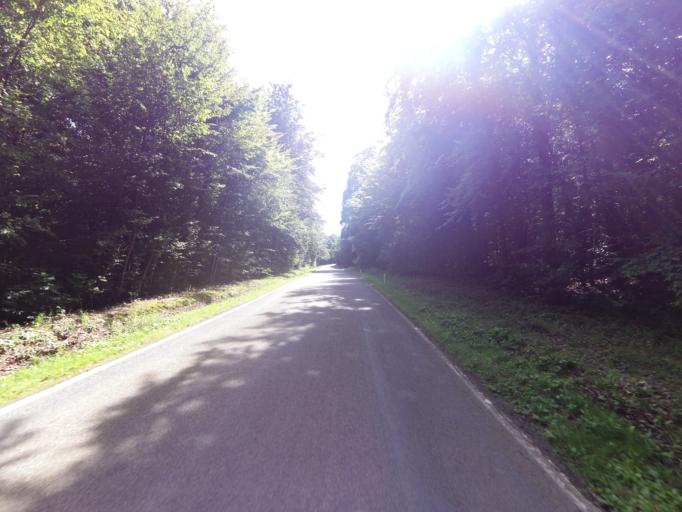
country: BE
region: Wallonia
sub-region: Province du Luxembourg
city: Nassogne
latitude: 50.0761
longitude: 5.3454
